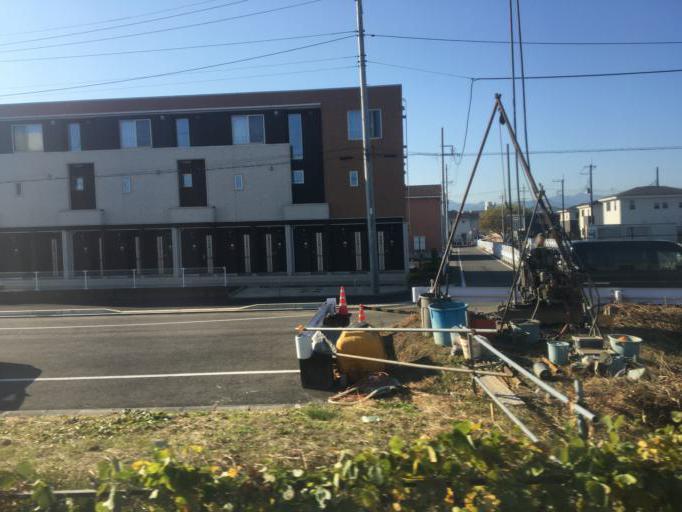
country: JP
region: Gunma
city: Takasaki
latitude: 36.3068
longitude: 139.0315
